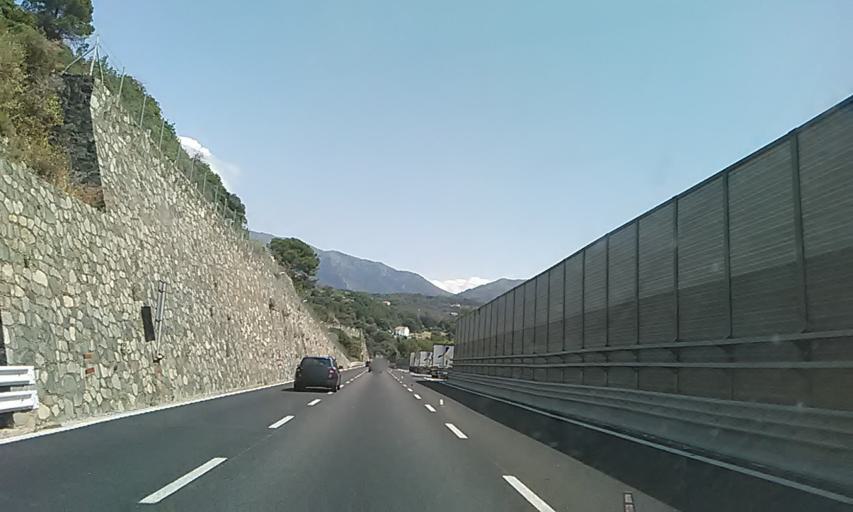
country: IT
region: Liguria
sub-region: Provincia di Genova
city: Cogoleto
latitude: 44.3844
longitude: 8.6341
